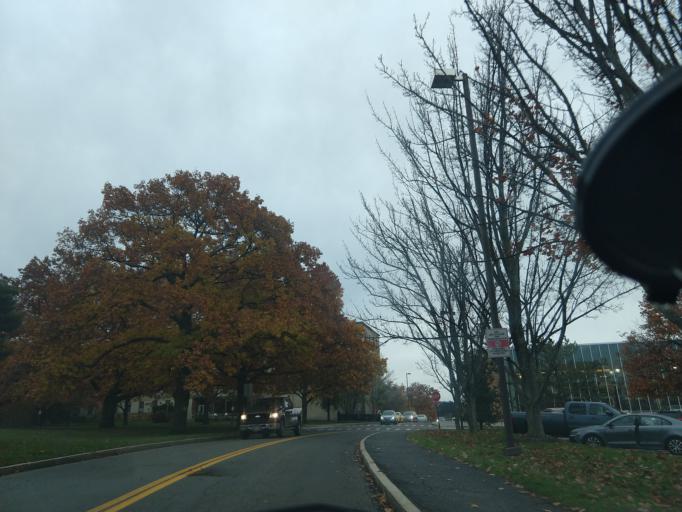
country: US
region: New York
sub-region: Tompkins County
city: East Ithaca
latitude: 42.4481
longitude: -76.4701
